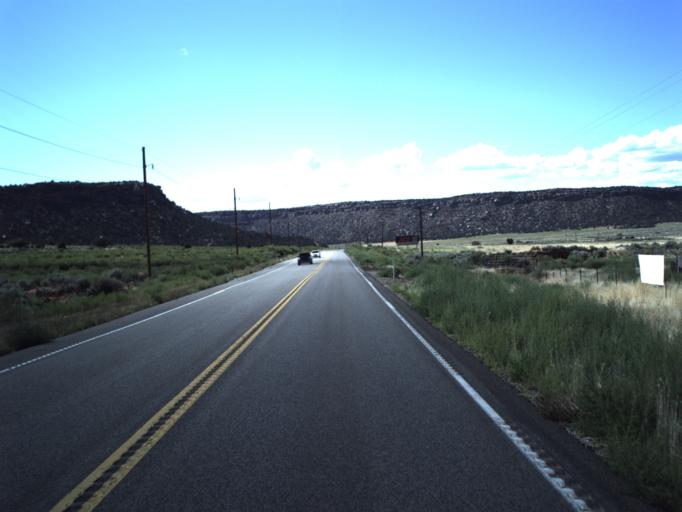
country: US
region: Utah
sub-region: Washington County
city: LaVerkin
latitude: 37.1069
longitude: -113.1403
